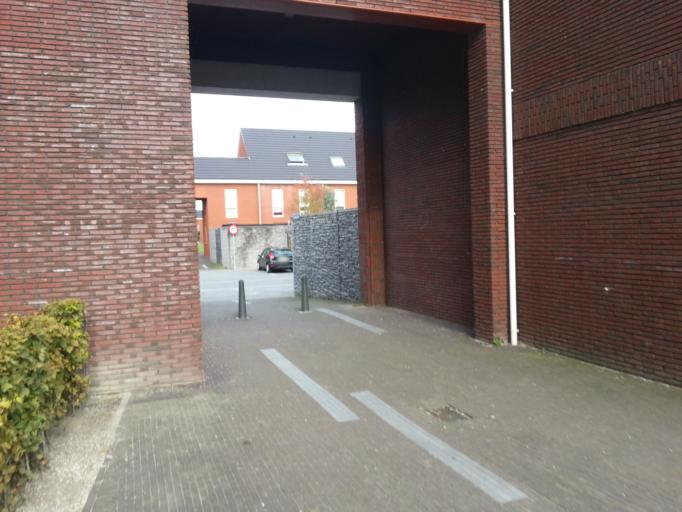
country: NL
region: South Holland
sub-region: Gemeente Den Haag
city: Ypenburg
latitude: 52.0464
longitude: 4.3815
